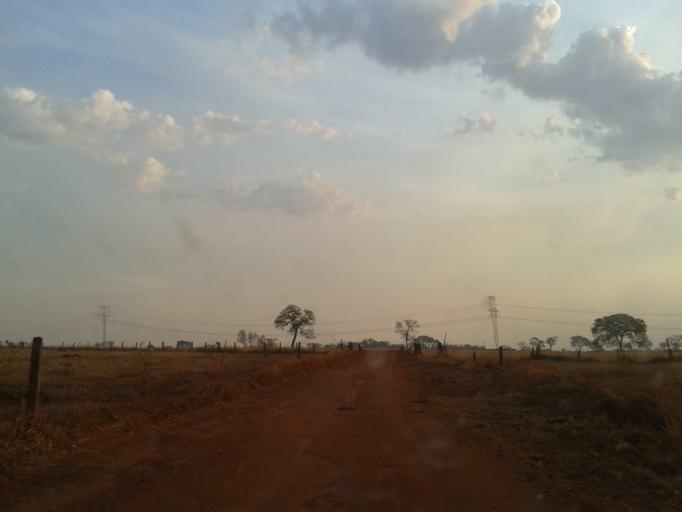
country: BR
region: Minas Gerais
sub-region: Capinopolis
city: Capinopolis
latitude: -18.8137
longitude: -49.7276
